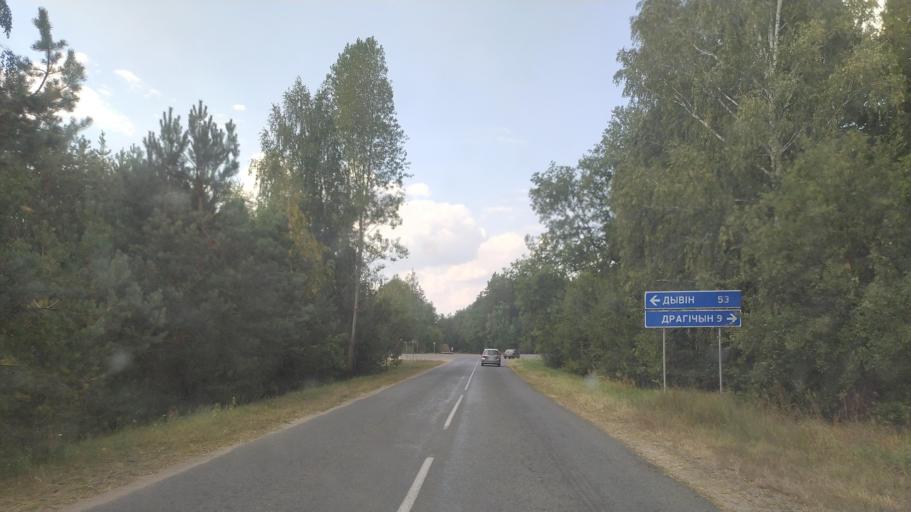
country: BY
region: Brest
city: Drahichyn
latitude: 52.1066
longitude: 25.1160
